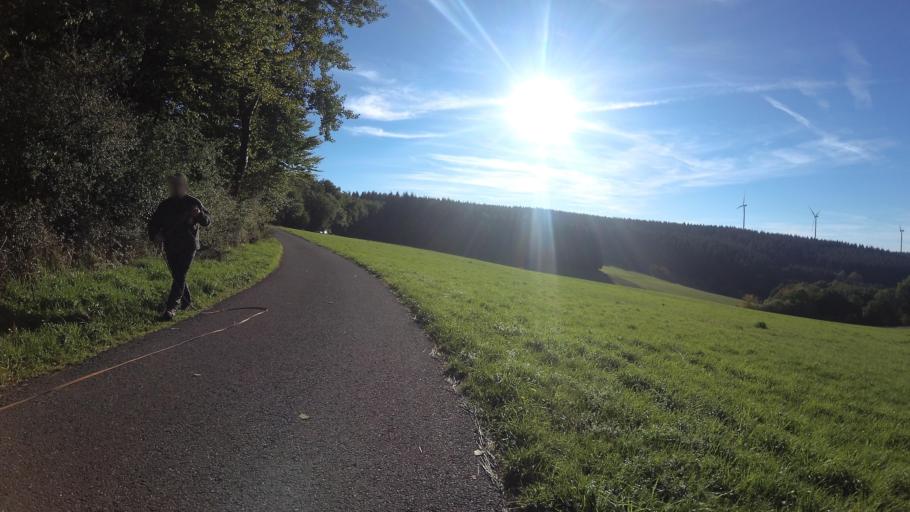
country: DE
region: Saarland
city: Freisen
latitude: 49.5410
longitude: 7.2479
